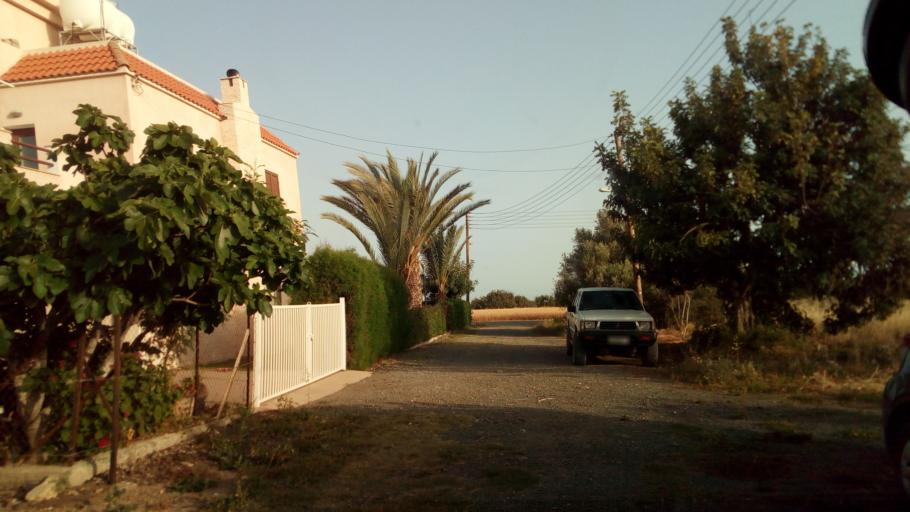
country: CY
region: Larnaka
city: Tersefanou
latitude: 34.8059
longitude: 33.5103
